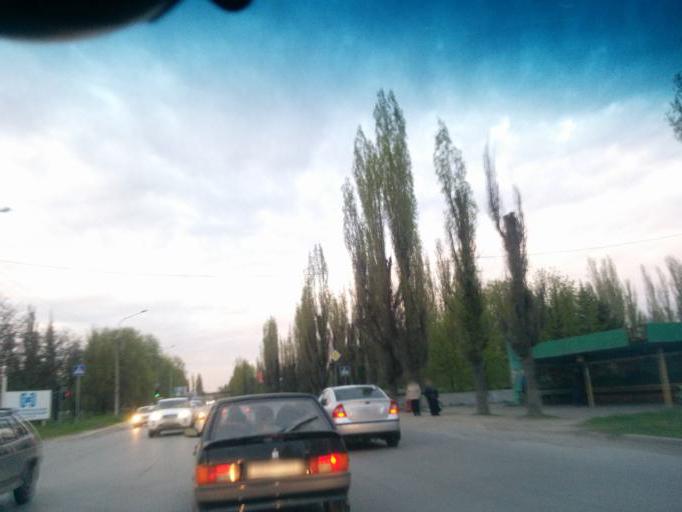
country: RU
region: Rostov
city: Novocherkassk
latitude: 47.4741
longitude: 40.1016
